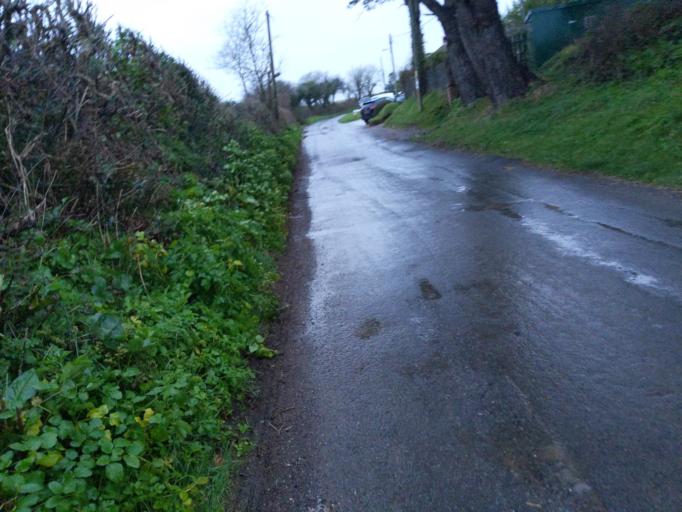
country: GB
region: England
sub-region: Devon
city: Yealmpton
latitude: 50.3220
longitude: -4.0323
